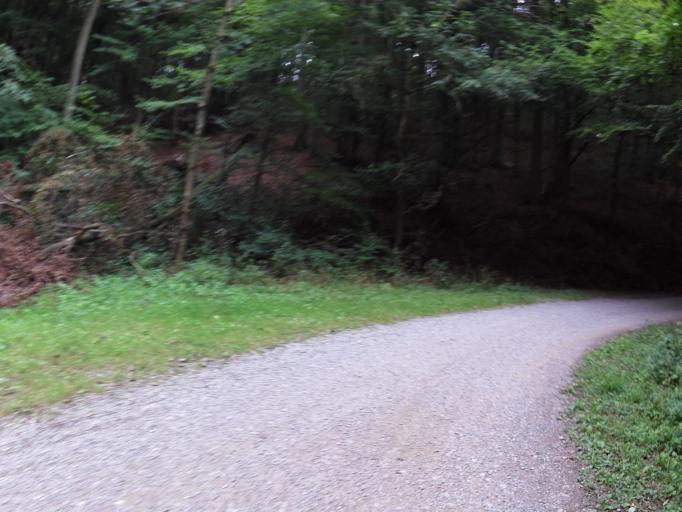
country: DE
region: North Rhine-Westphalia
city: Heimbach
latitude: 50.6280
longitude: 6.4193
